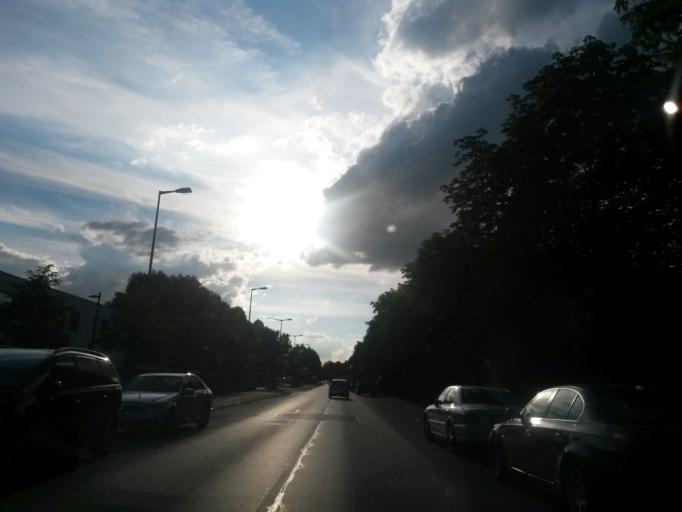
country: DE
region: Bavaria
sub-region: Upper Bavaria
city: Neubiberg
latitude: 48.0974
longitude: 11.6428
